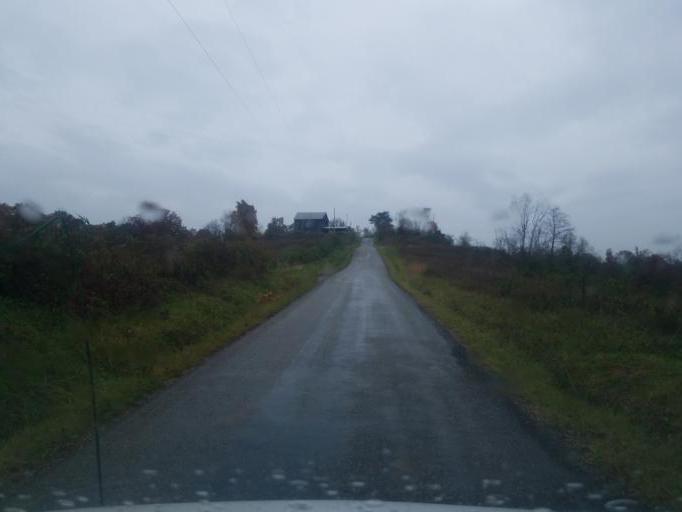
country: US
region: Ohio
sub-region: Washington County
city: Belpre
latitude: 39.3185
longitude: -81.6047
